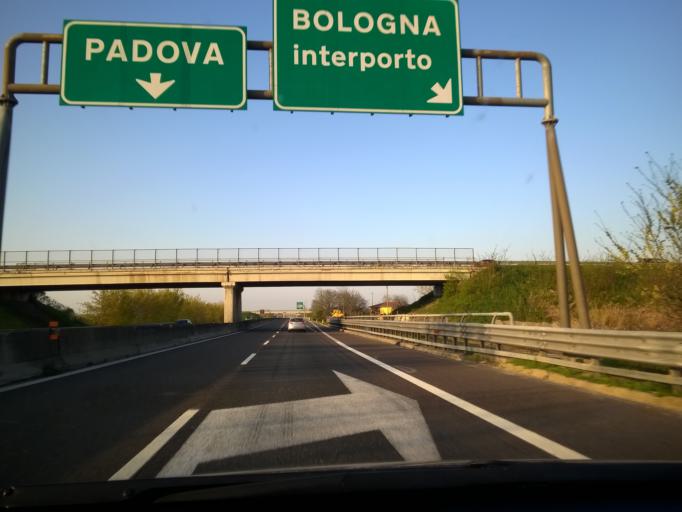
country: IT
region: Emilia-Romagna
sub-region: Provincia di Bologna
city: Progresso
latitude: 44.5880
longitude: 11.3980
